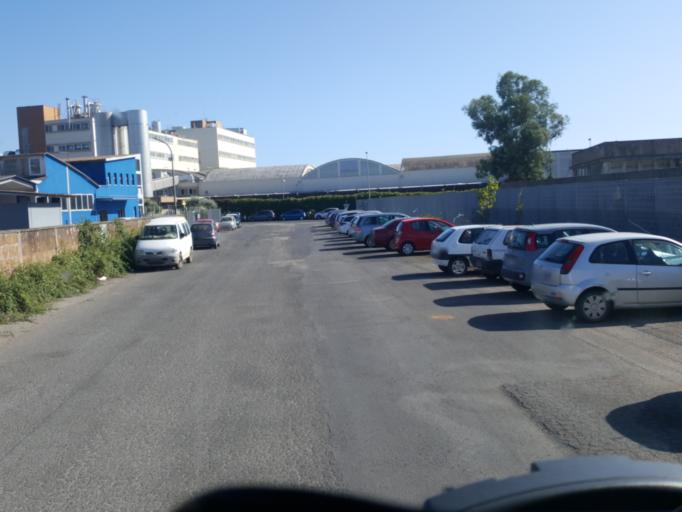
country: IT
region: Latium
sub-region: Citta metropolitana di Roma Capitale
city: Anzio
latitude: 41.5144
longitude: 12.6256
